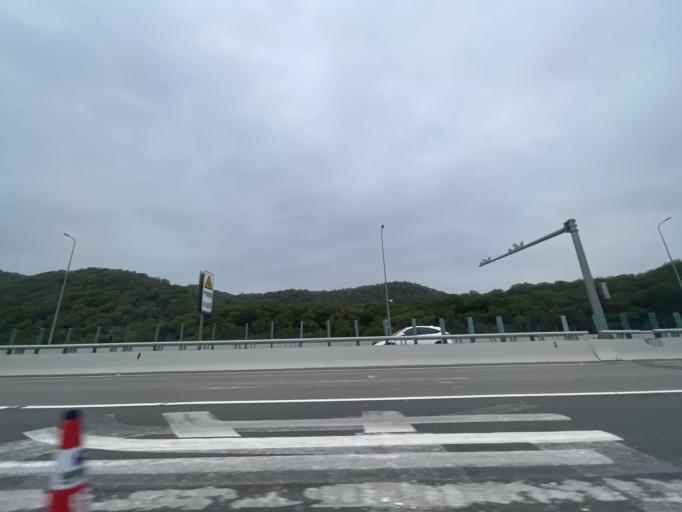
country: CN
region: Guangdong
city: Xinwan
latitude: 22.8047
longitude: 113.6288
